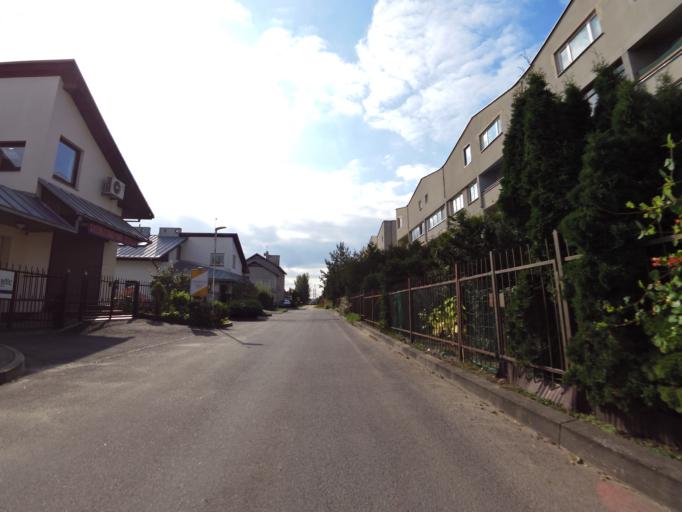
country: LT
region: Vilnius County
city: Pilaite
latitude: 54.7007
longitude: 25.1725
